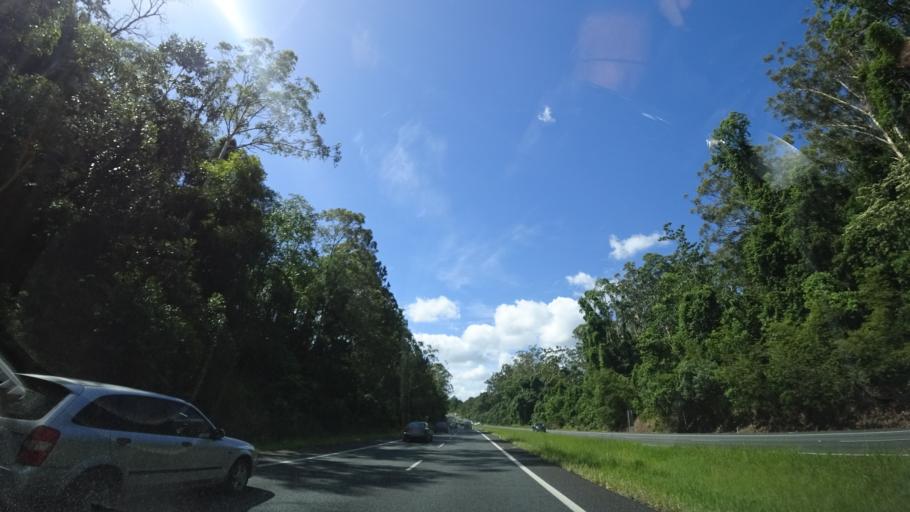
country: AU
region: Queensland
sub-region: Sunshine Coast
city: Woombye
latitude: -26.6676
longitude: 152.9971
